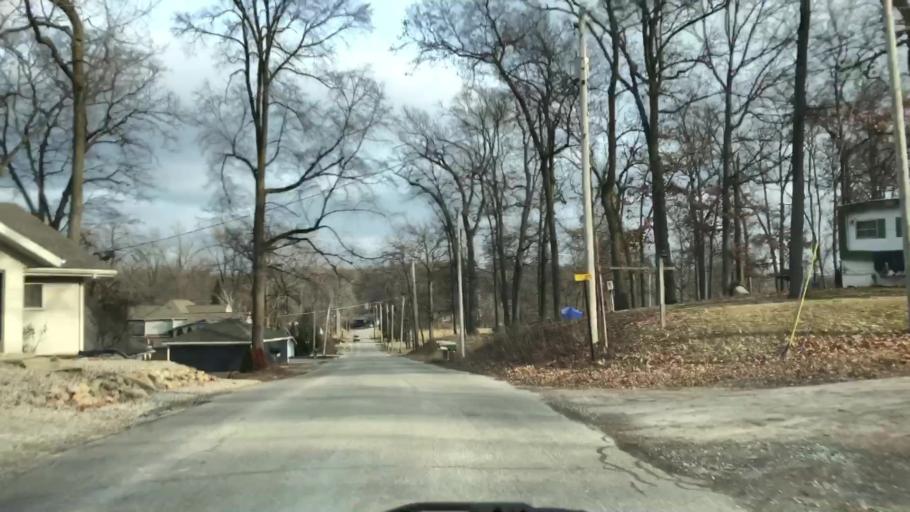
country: US
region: Indiana
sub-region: Steuben County
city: Angola
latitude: 41.6809
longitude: -85.0236
